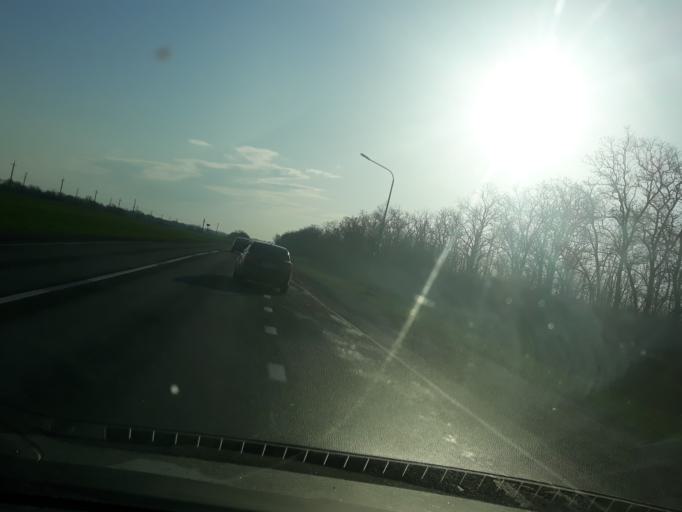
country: RU
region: Rostov
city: Novobessergenovka
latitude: 47.1889
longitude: 38.6226
